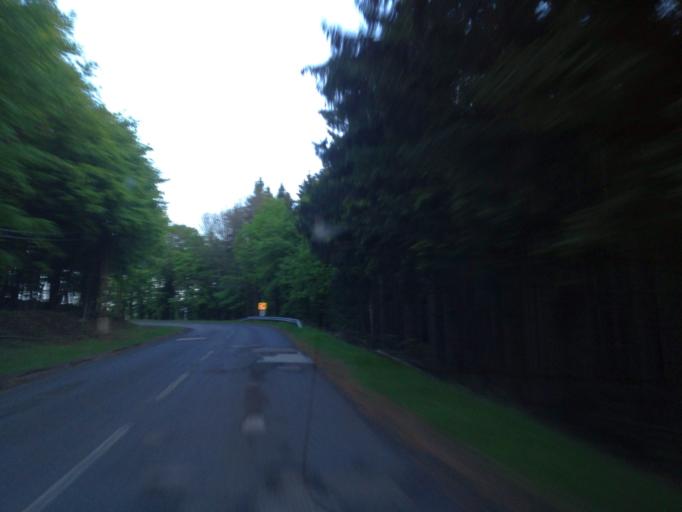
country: HU
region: Nograd
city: Batonyterenye
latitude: 47.8952
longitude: 19.8588
